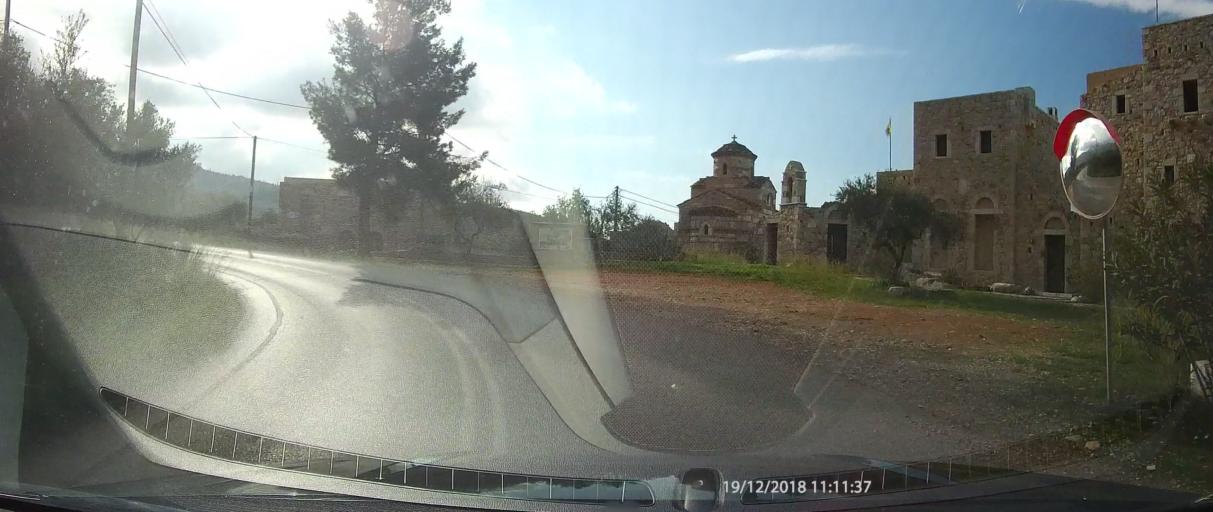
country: GR
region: Peloponnese
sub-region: Nomos Messinias
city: Kardamyli
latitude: 36.8188
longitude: 22.3014
